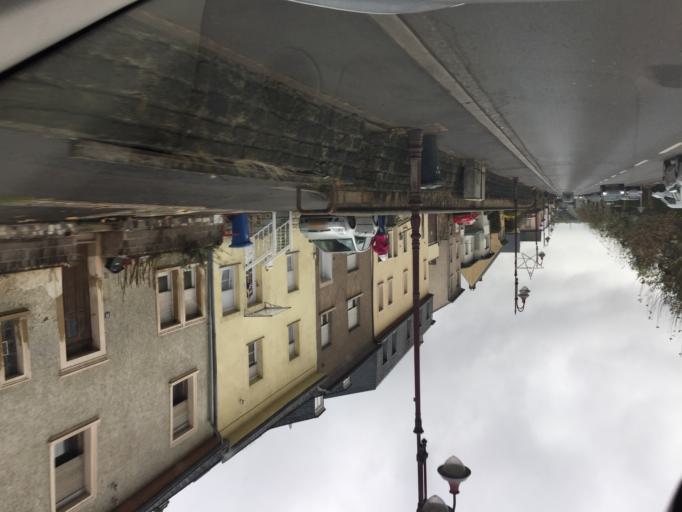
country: LU
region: Diekirch
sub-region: Canton de Diekirch
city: Diekirch
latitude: 49.8687
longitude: 6.1712
